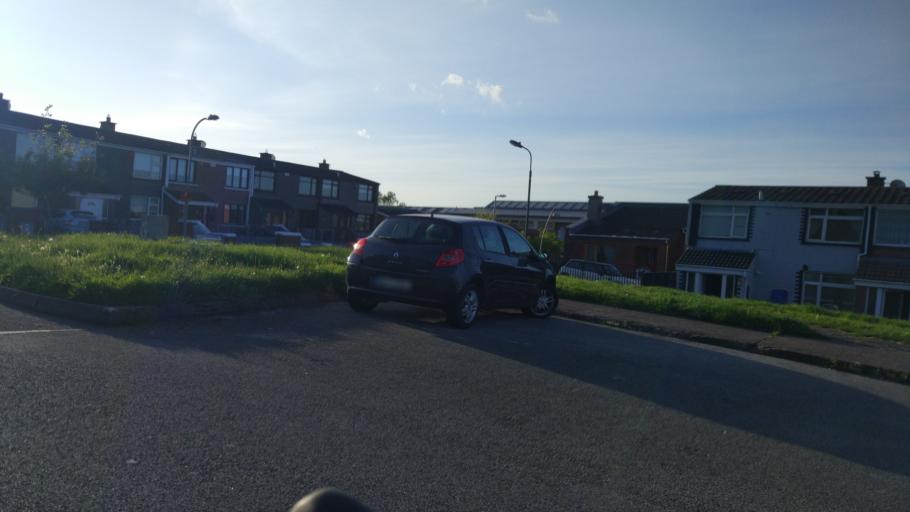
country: IE
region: Munster
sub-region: County Cork
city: Cork
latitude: 51.9121
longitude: -8.4604
